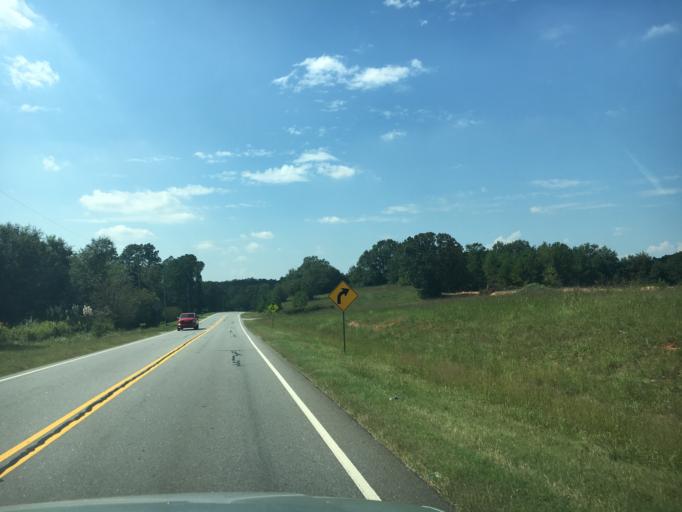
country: US
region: Georgia
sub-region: Hart County
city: Hartwell
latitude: 34.3618
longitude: -82.9694
